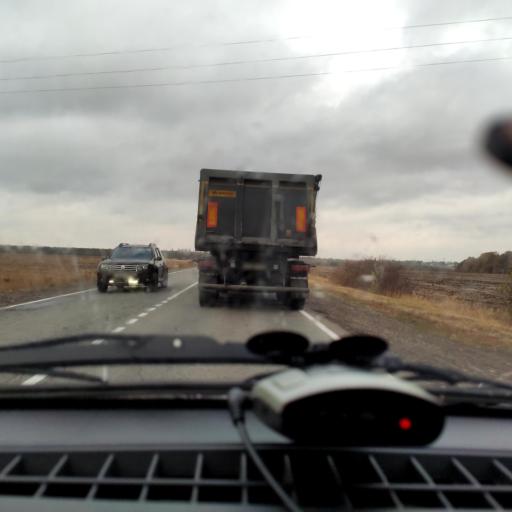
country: RU
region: Voronezj
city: Shilovo
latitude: 51.4476
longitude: 38.9921
